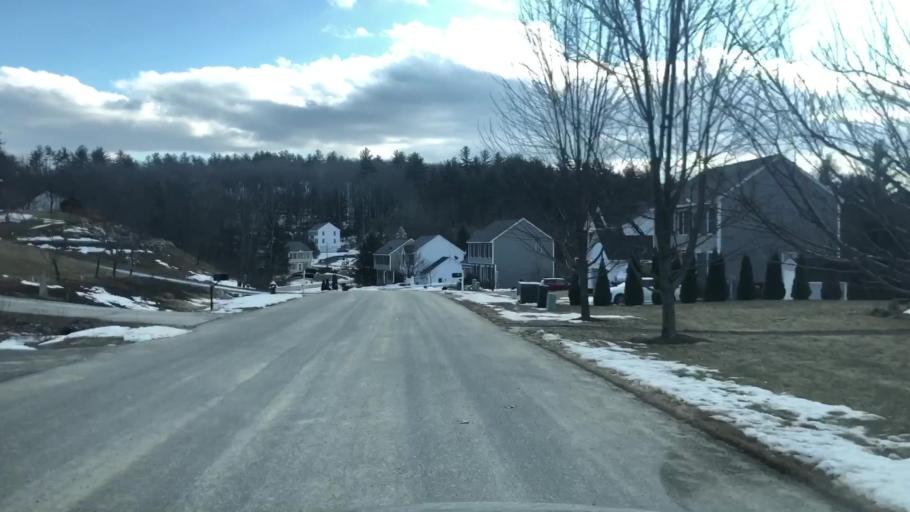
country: US
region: New Hampshire
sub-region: Hillsborough County
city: Milford
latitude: 42.8492
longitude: -71.6576
